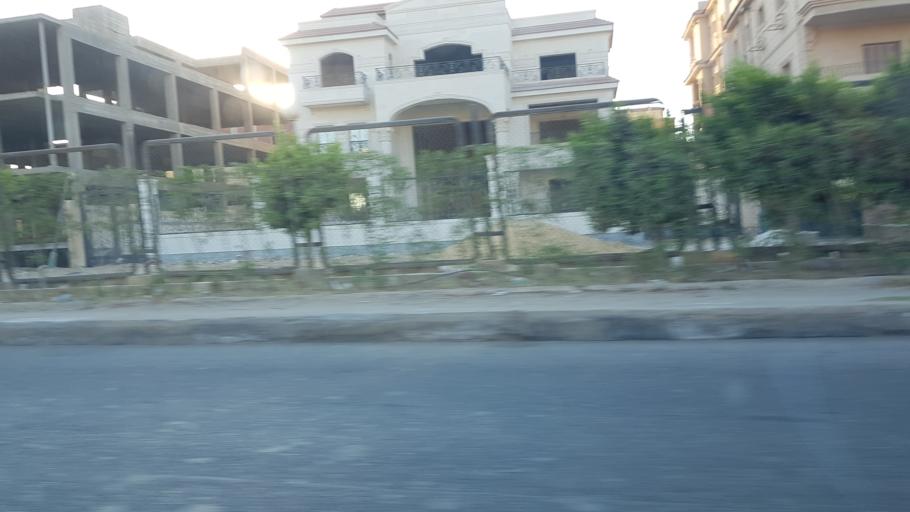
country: EG
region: Muhafazat al Qalyubiyah
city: Al Khankah
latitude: 30.0623
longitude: 31.4452
